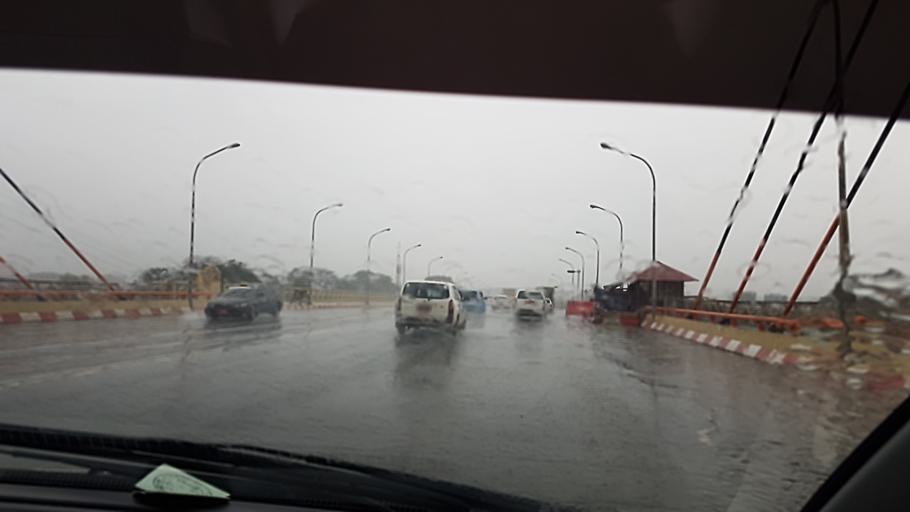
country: MM
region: Yangon
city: Yangon
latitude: 16.7775
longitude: 96.1836
